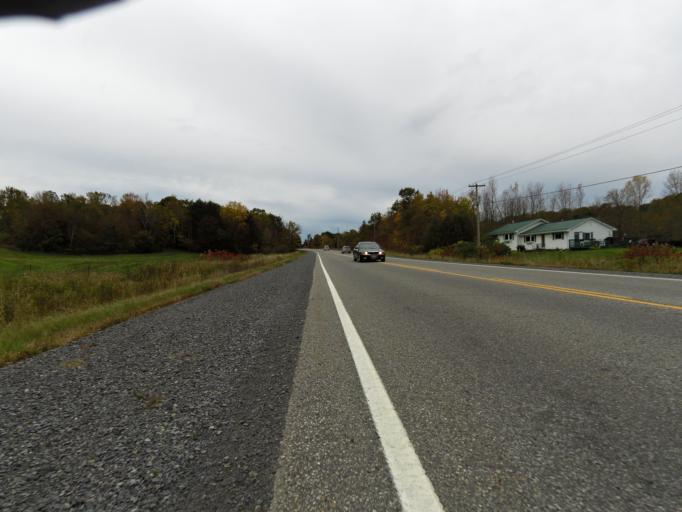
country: CA
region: Ontario
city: Gananoque
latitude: 44.4208
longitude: -76.3023
